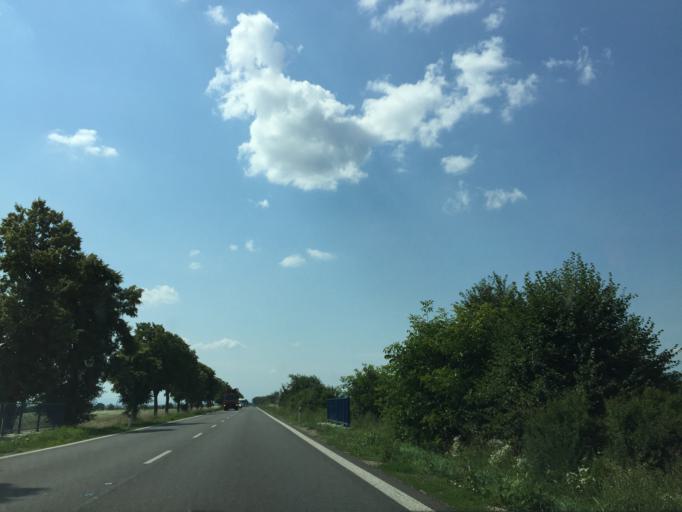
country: SK
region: Kosicky
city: Sobrance
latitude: 48.7573
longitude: 22.1392
